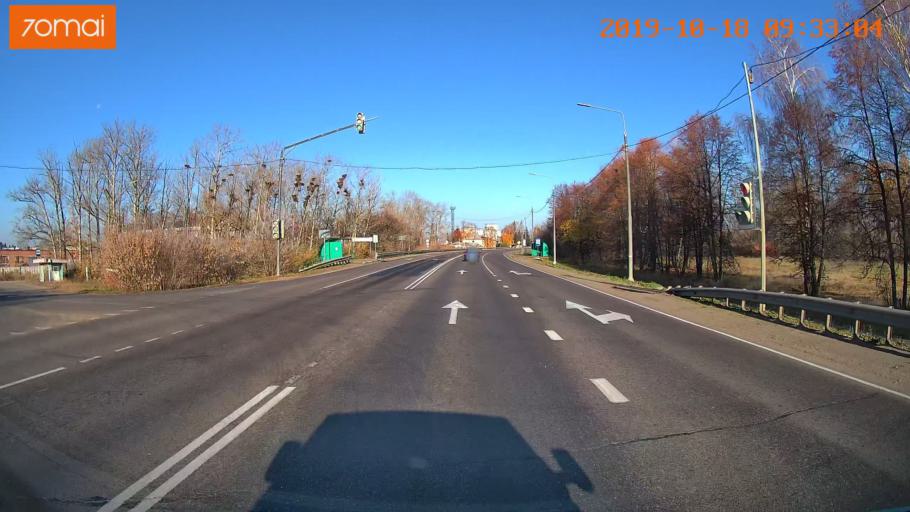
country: RU
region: Tula
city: Yefremov
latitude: 53.1630
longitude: 38.1533
